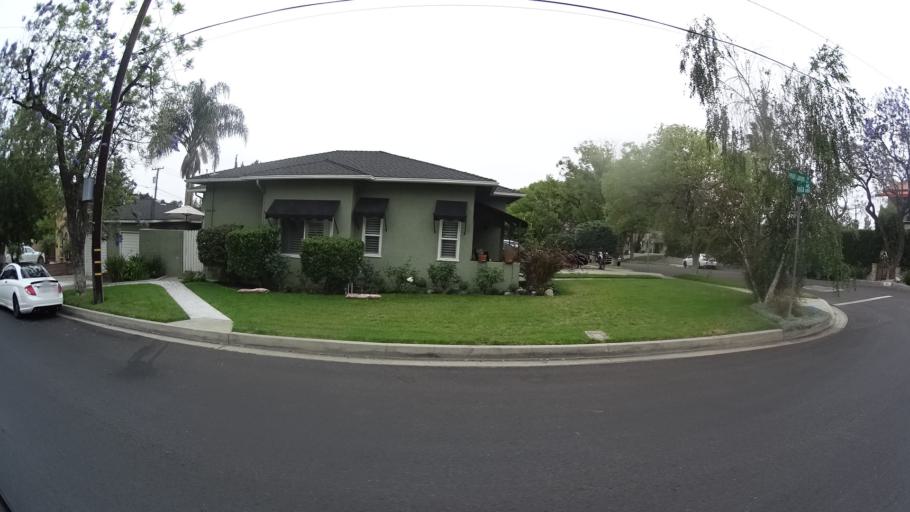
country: US
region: California
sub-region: Los Angeles County
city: Burbank
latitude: 34.1894
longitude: -118.2924
